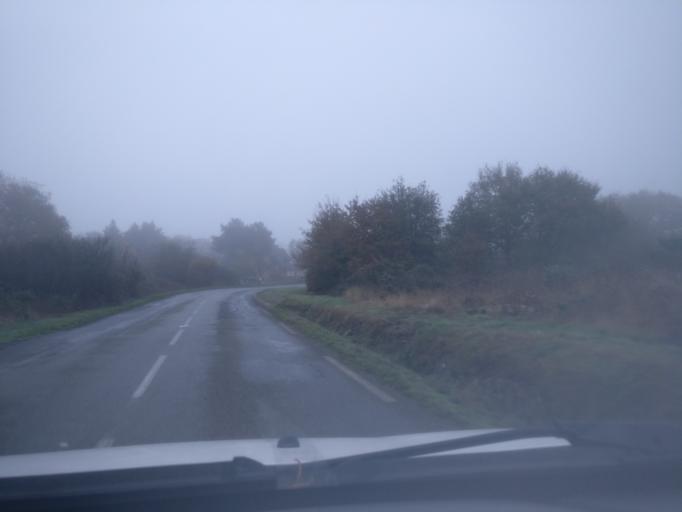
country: FR
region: Brittany
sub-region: Departement d'Ille-et-Vilaine
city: Bruz
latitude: 47.9984
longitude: -1.7361
